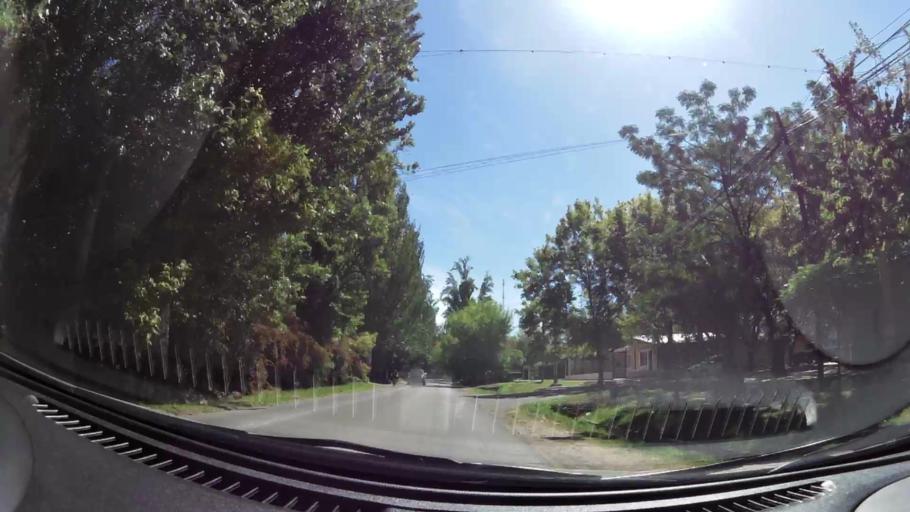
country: AR
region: Mendoza
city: Lujan de Cuyo
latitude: -32.9830
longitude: -68.8571
